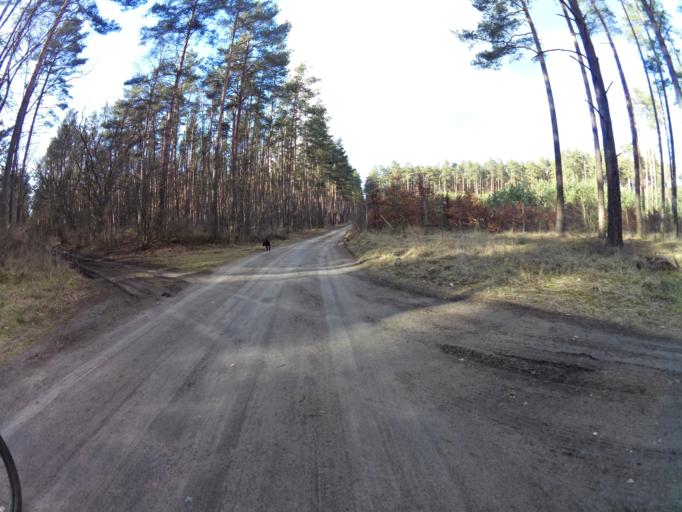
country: PL
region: West Pomeranian Voivodeship
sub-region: Powiat mysliborski
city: Debno
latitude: 52.7944
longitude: 14.7481
